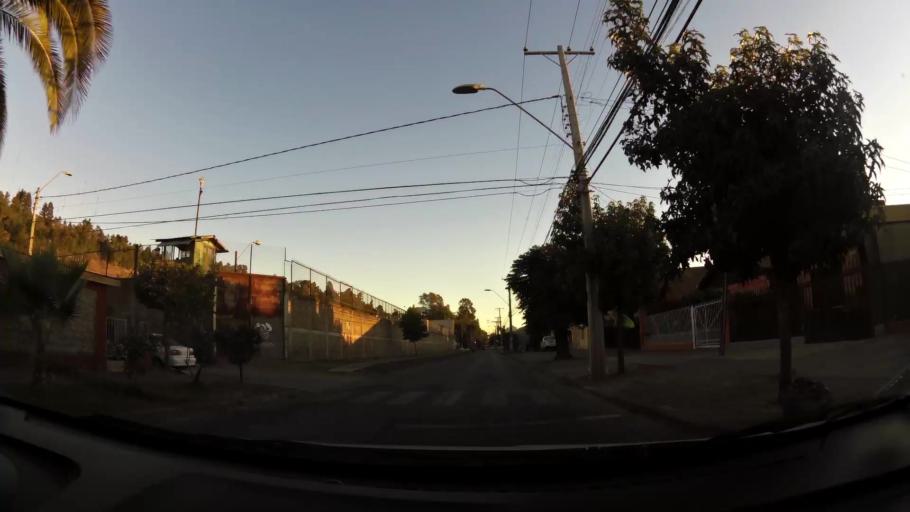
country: CL
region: Maule
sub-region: Provincia de Curico
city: Curico
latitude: -34.9791
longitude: -71.2351
